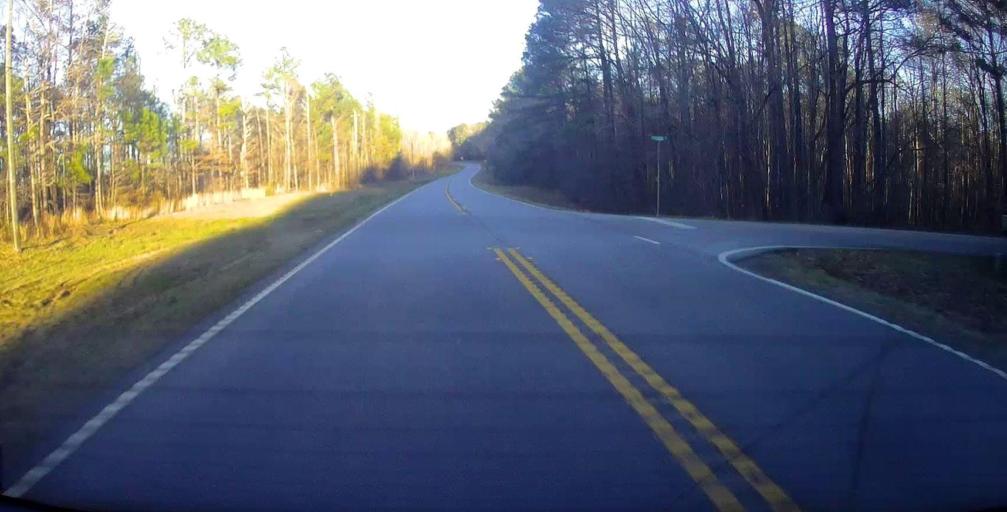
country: US
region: Georgia
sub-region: Harris County
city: Hamilton
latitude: 32.6728
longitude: -84.9268
